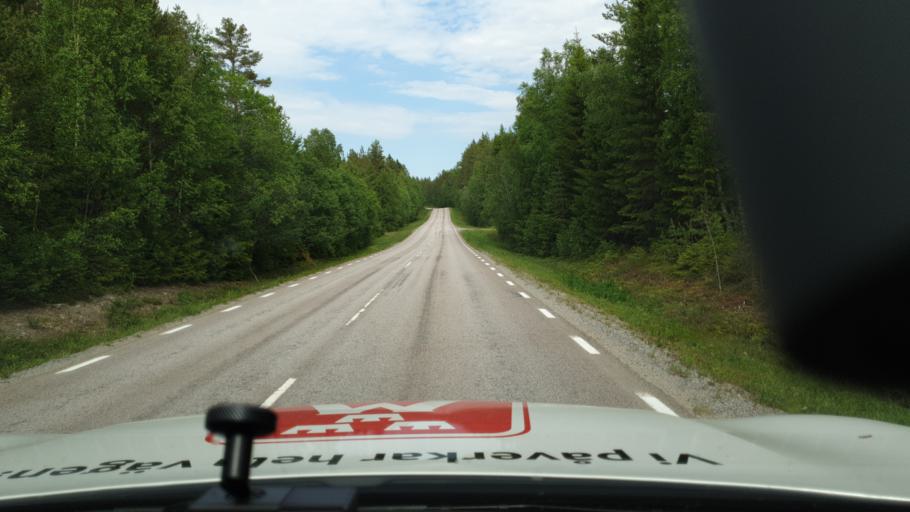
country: SE
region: Vaesterbotten
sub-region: Umea Kommun
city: Hoernefors
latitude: 63.6091
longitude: 19.8688
